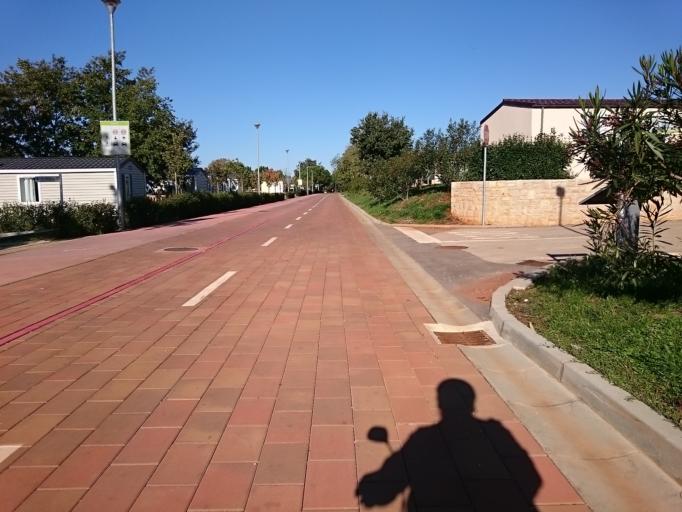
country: HR
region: Istarska
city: Novigrad
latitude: 45.3634
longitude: 13.5470
